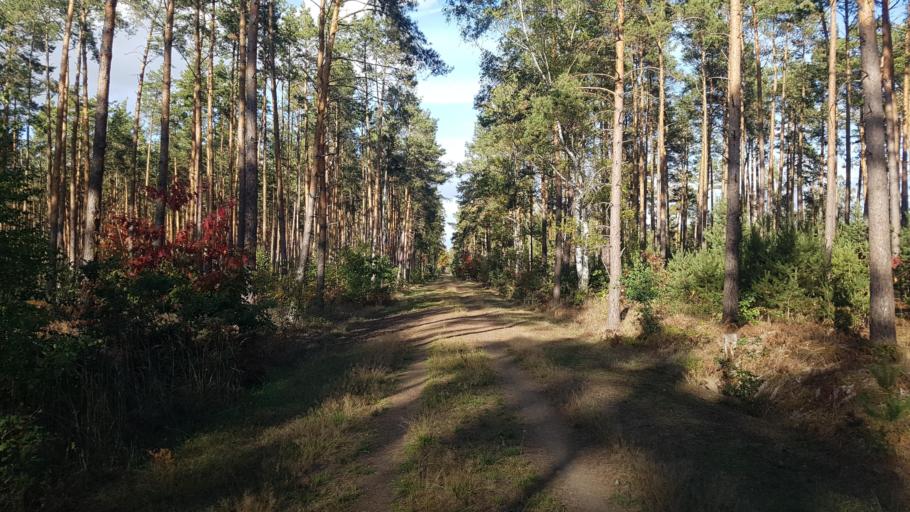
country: DE
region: Brandenburg
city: Bad Liebenwerda
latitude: 51.4890
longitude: 13.3025
